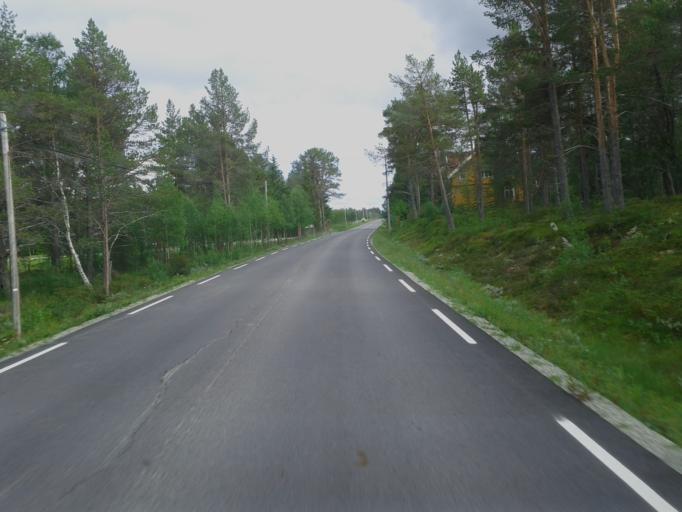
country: NO
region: Sor-Trondelag
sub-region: Roros
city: Roros
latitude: 62.2966
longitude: 11.7258
